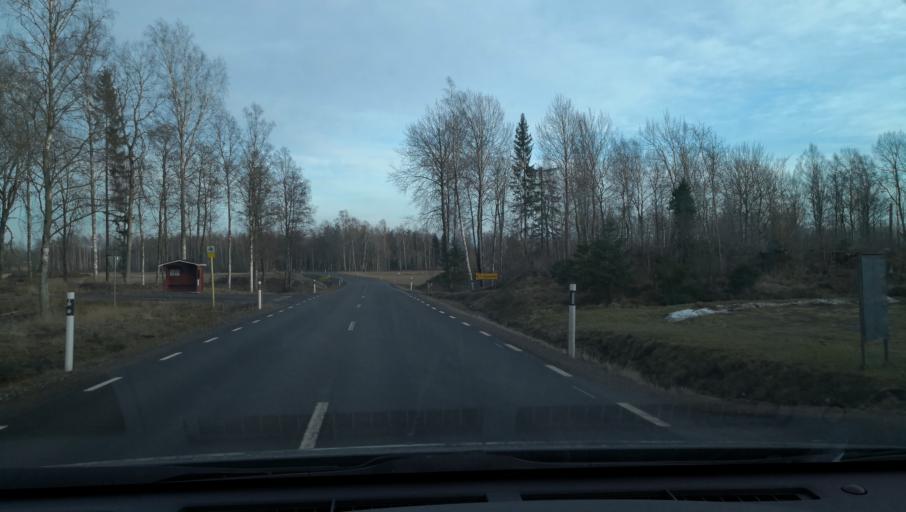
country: SE
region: Vaestra Goetaland
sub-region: Gullspangs Kommun
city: Gullspang
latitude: 59.0549
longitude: 14.2413
